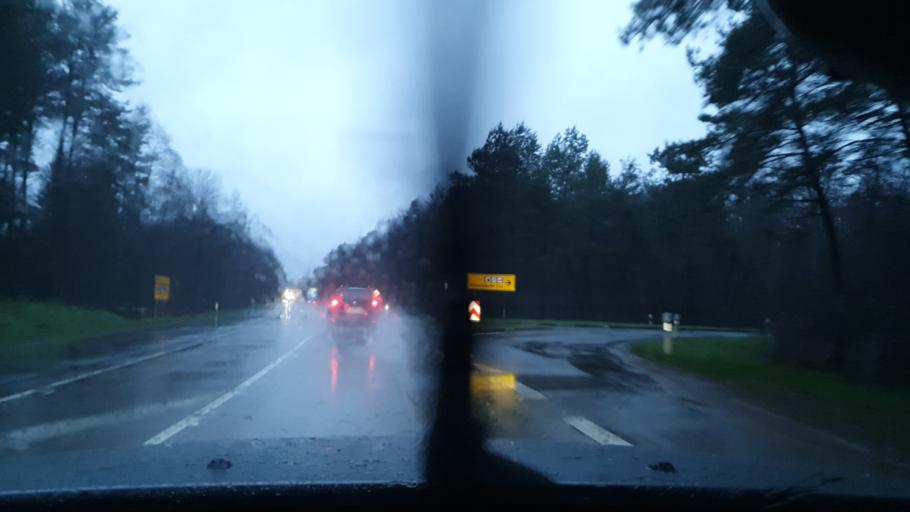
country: DE
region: Rheinland-Pfalz
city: Bechhofen
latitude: 49.3667
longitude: 7.3775
